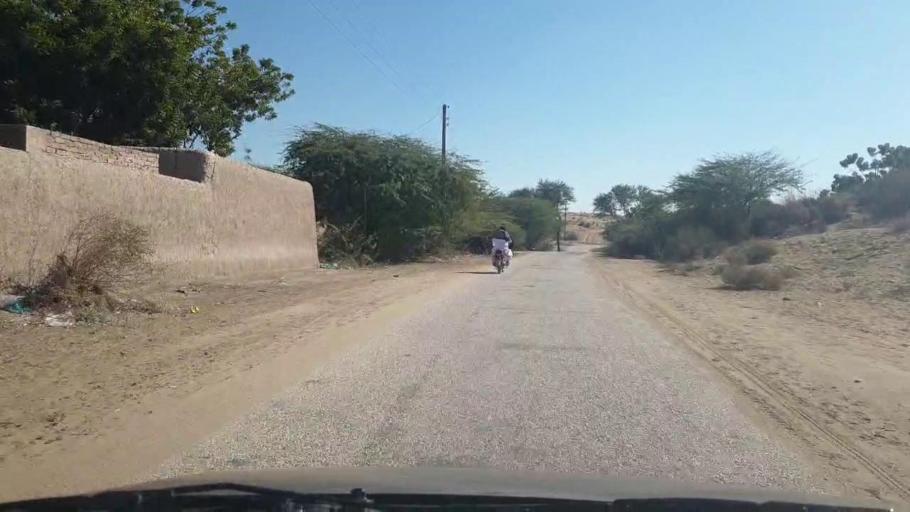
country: PK
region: Sindh
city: Bozdar
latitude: 27.0562
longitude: 68.6463
